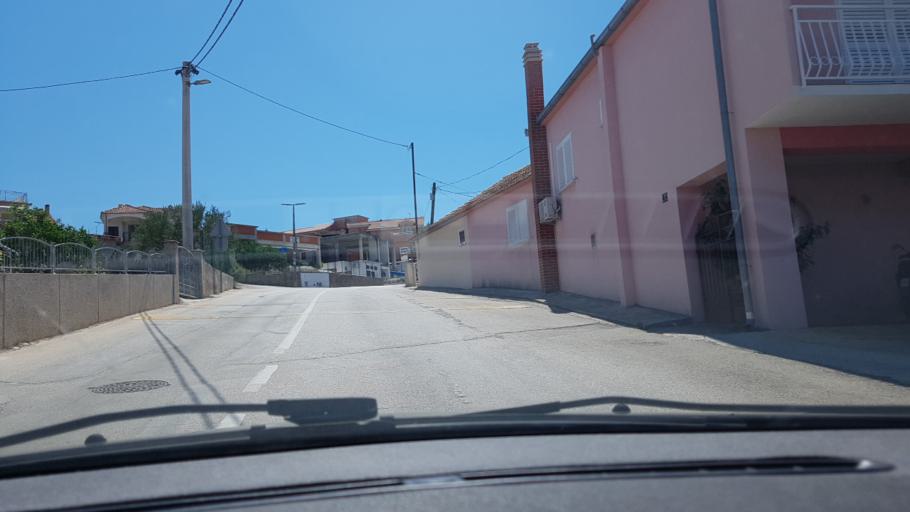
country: HR
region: Splitsko-Dalmatinska
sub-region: Grad Trogir
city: Trogir
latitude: 43.4952
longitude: 16.2630
